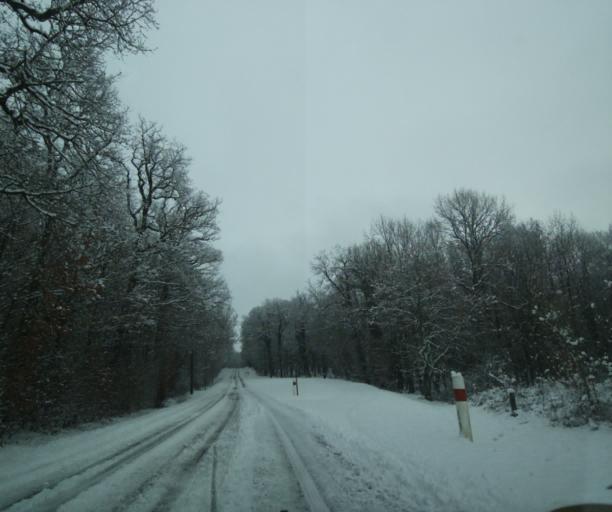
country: FR
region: Champagne-Ardenne
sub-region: Departement de la Haute-Marne
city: Montier-en-Der
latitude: 48.5436
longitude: 4.8014
